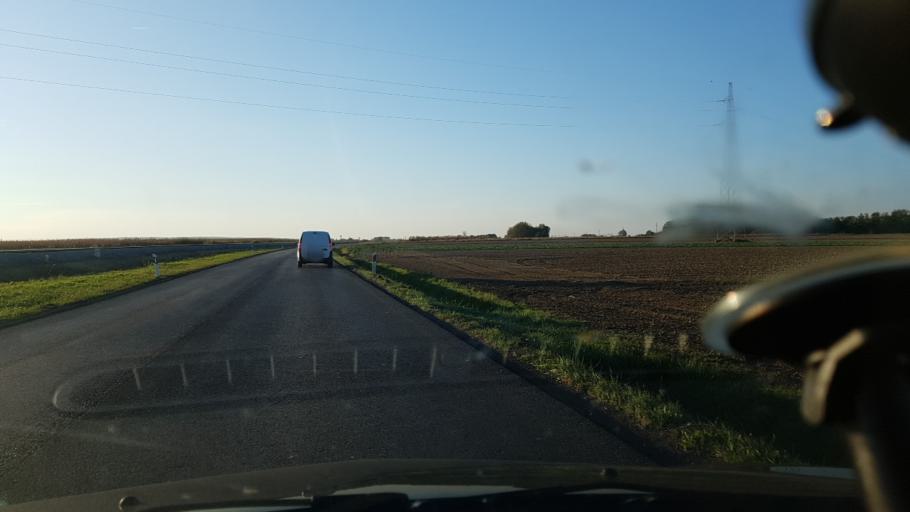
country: HR
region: Koprivnicko-Krizevacka
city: Virje
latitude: 46.0508
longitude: 17.0322
